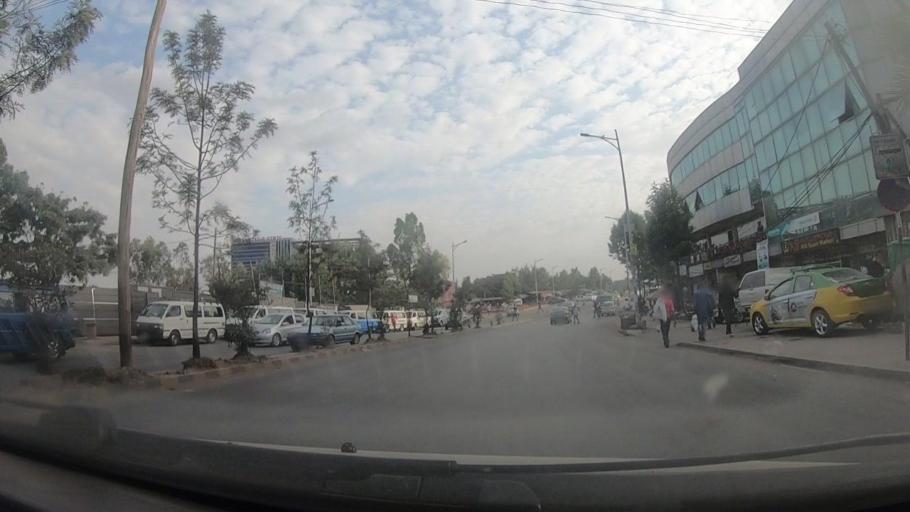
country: ET
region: Adis Abeba
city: Addis Ababa
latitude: 8.9656
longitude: 38.7328
